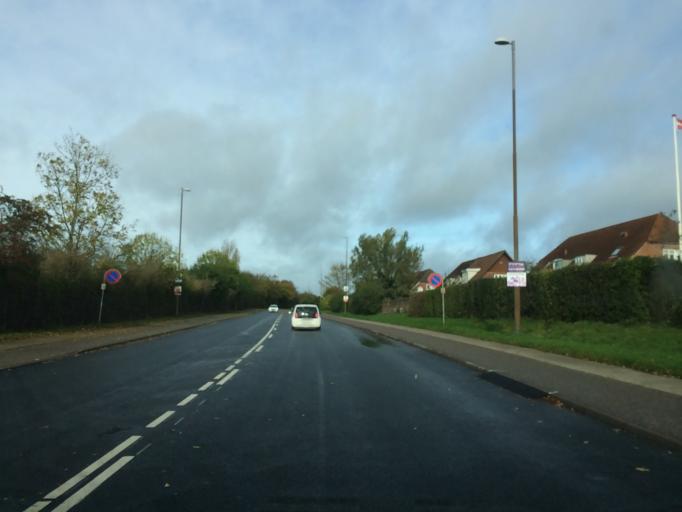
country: DK
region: South Denmark
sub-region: Fredericia Kommune
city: Fredericia
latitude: 55.5701
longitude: 9.7429
